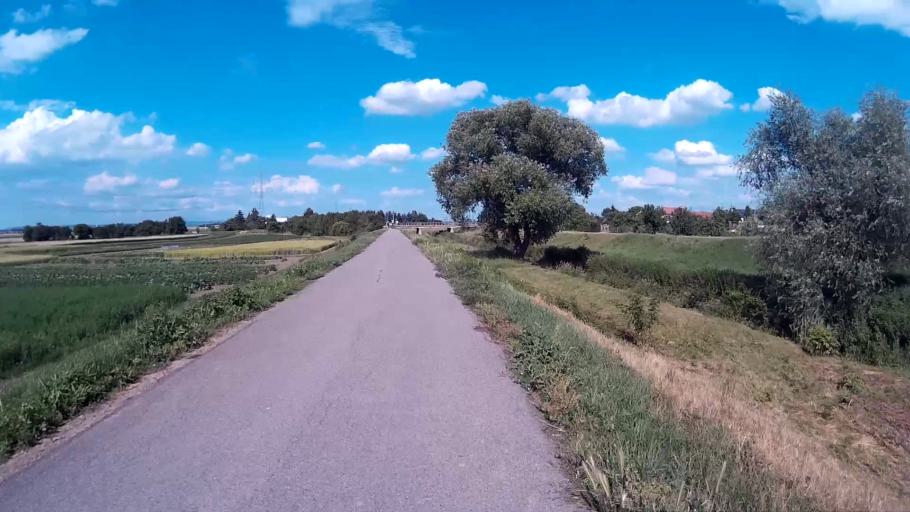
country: CZ
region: South Moravian
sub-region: Okres Brno-Venkov
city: Blucina
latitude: 49.0570
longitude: 16.6420
